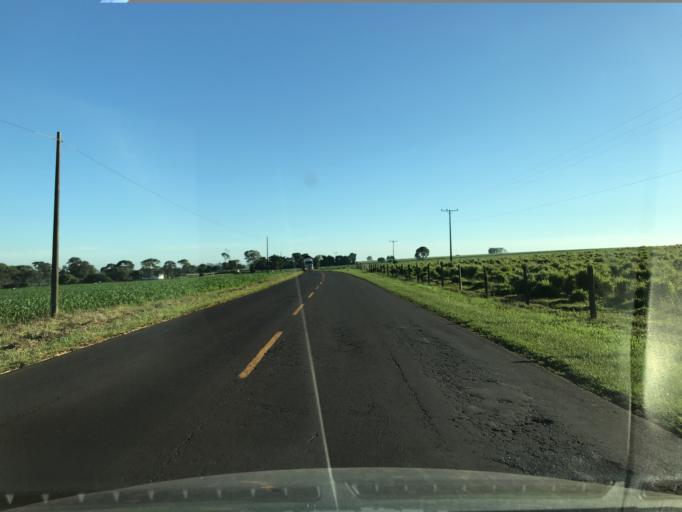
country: BR
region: Parana
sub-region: Ipora
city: Ipora
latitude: -24.1011
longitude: -53.8384
